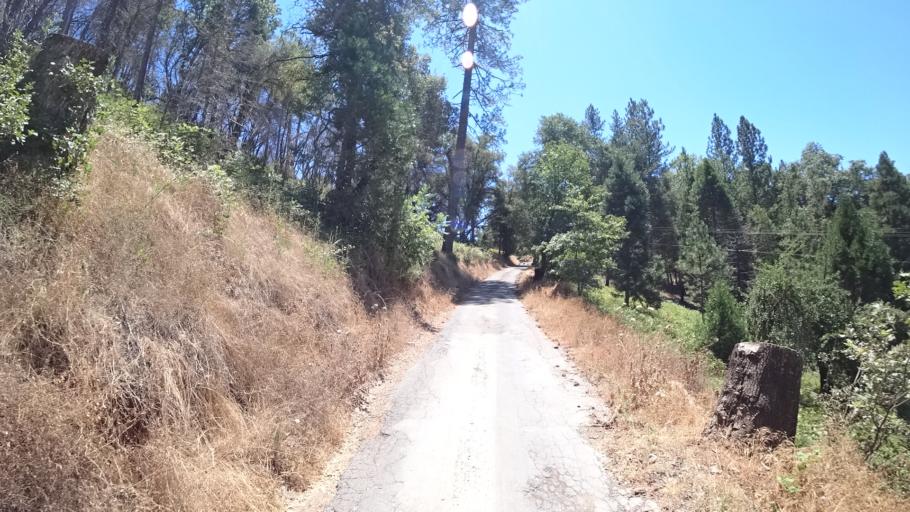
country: US
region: California
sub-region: Calaveras County
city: Mountain Ranch
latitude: 38.2683
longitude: -120.5854
